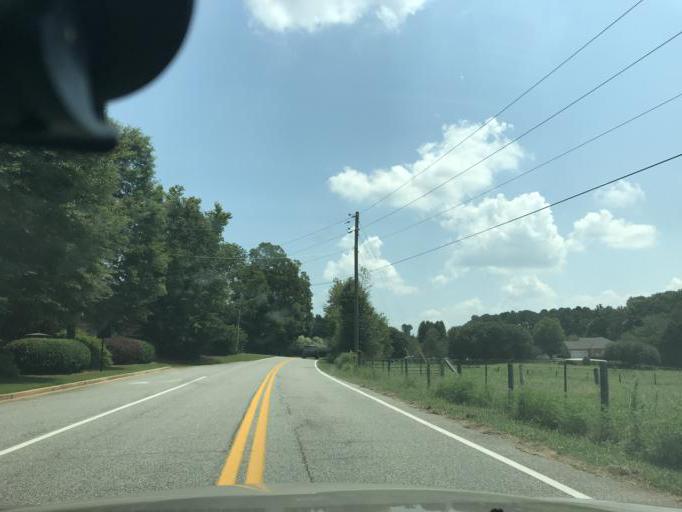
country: US
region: Georgia
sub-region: Dawson County
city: Dawsonville
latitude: 34.3167
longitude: -84.1492
